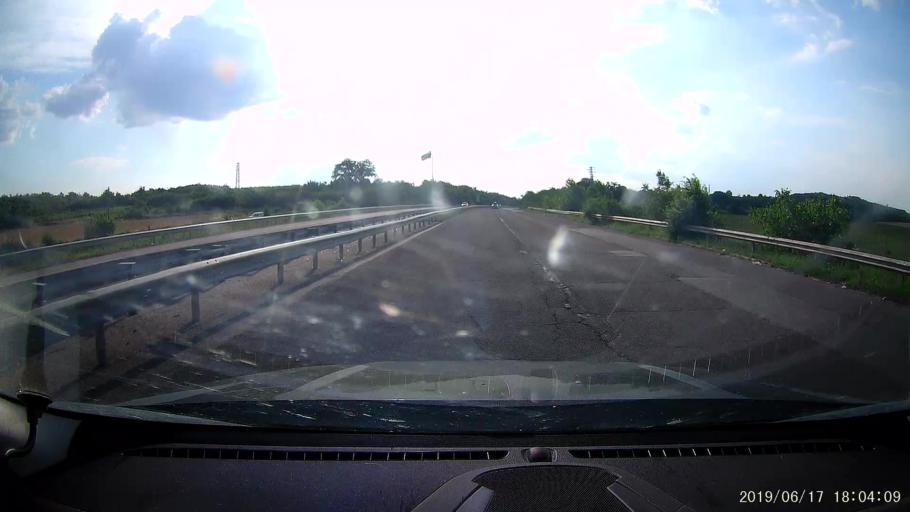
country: BG
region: Khaskovo
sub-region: Obshtina Svilengrad
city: Svilengrad
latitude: 41.7831
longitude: 26.2048
